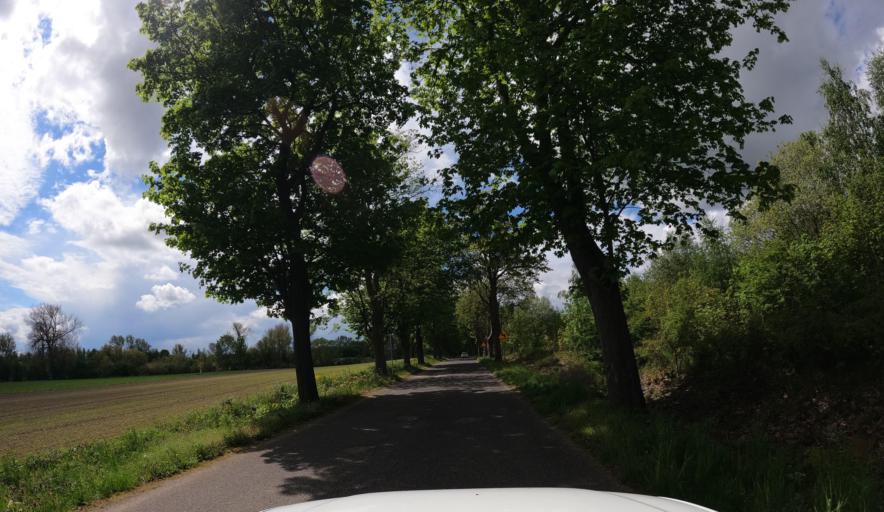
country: PL
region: West Pomeranian Voivodeship
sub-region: Powiat kamienski
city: Wolin
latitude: 53.8548
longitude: 14.6337
